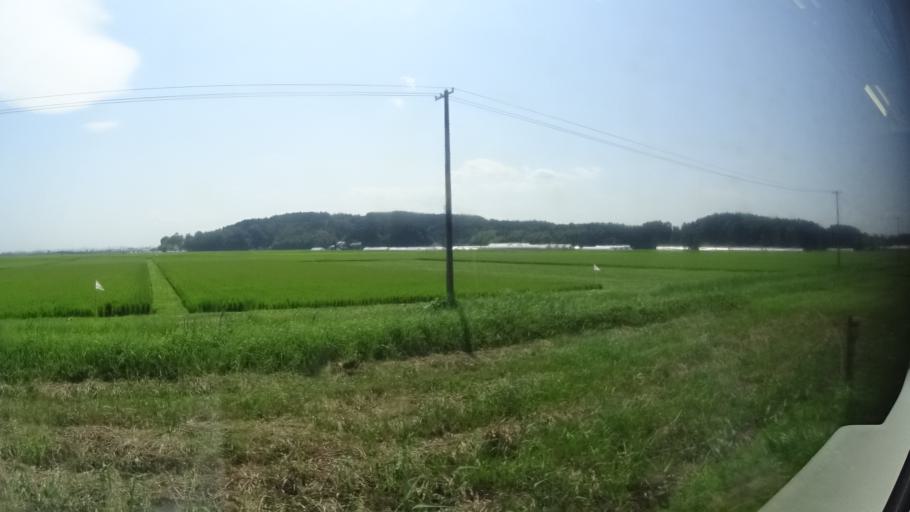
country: JP
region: Miyagi
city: Wakuya
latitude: 38.5233
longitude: 141.1618
